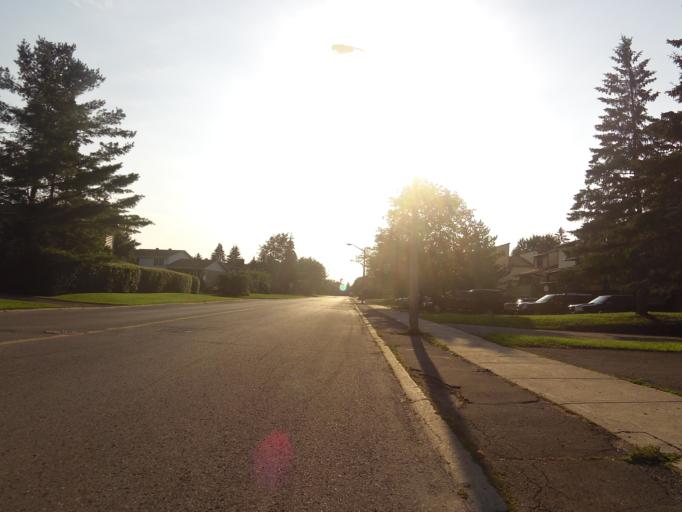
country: CA
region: Ontario
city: Bells Corners
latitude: 45.3324
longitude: -75.7887
